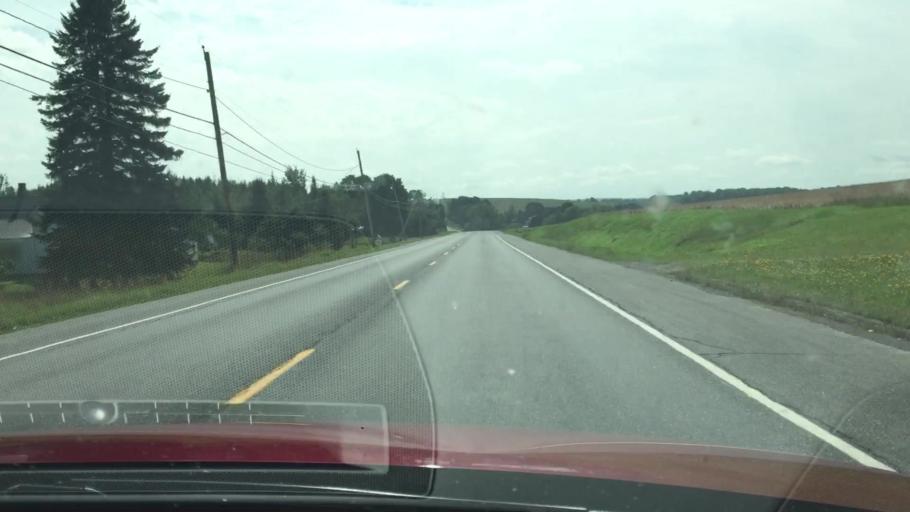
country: US
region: Maine
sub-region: Aroostook County
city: Easton
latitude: 46.5887
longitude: -67.9619
